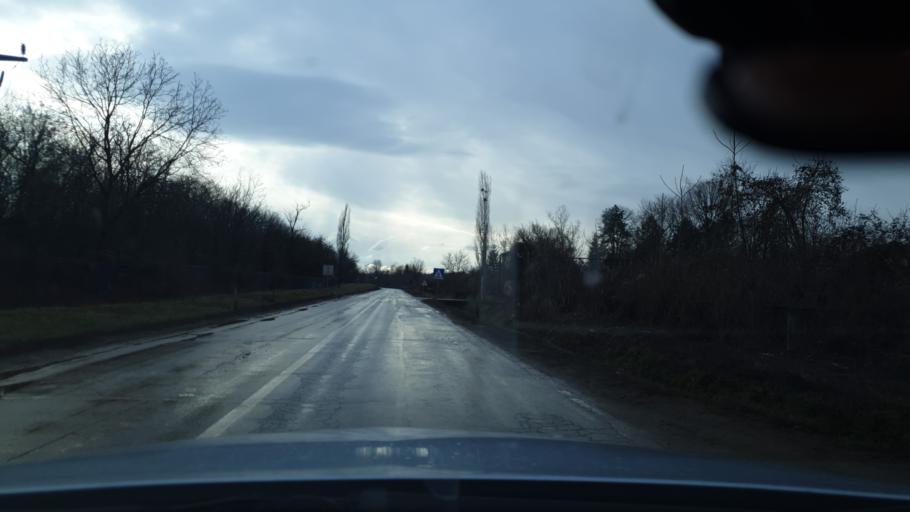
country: RS
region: Central Serbia
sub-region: Podunavski Okrug
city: Smederevo
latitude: 44.6014
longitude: 20.9634
